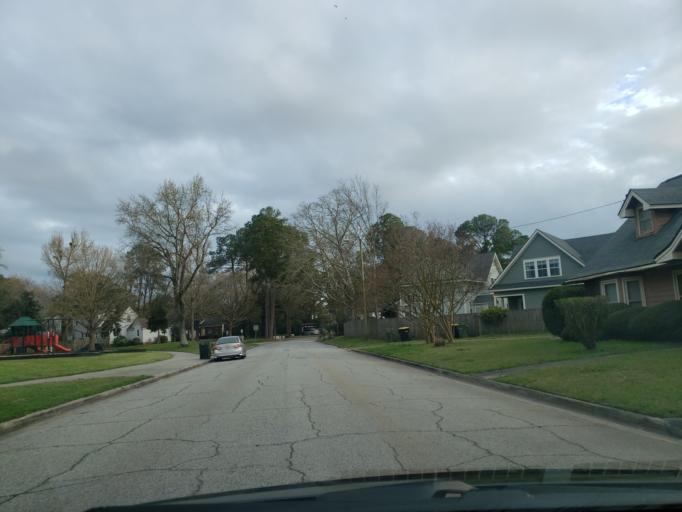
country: US
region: Georgia
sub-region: Chatham County
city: Savannah
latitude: 32.0408
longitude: -81.0955
